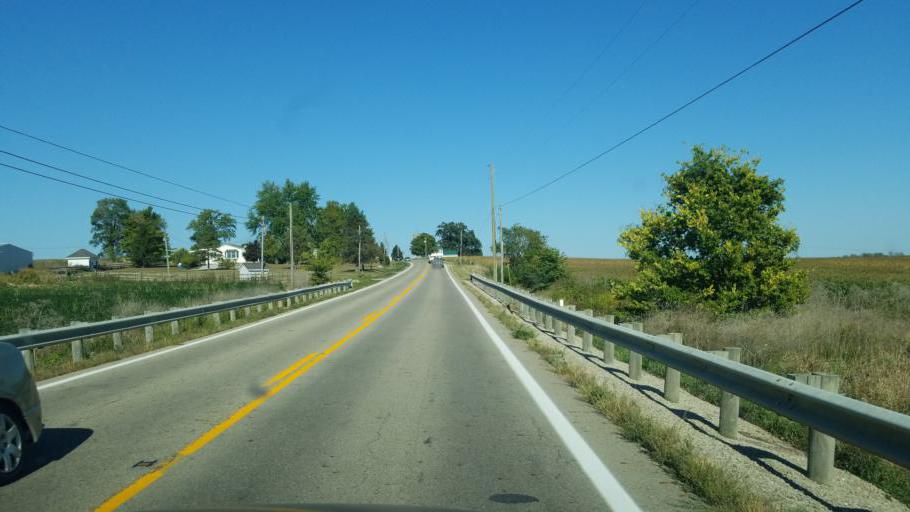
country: US
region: Ohio
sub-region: Champaign County
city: Mechanicsburg
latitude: 40.0815
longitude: -83.5420
